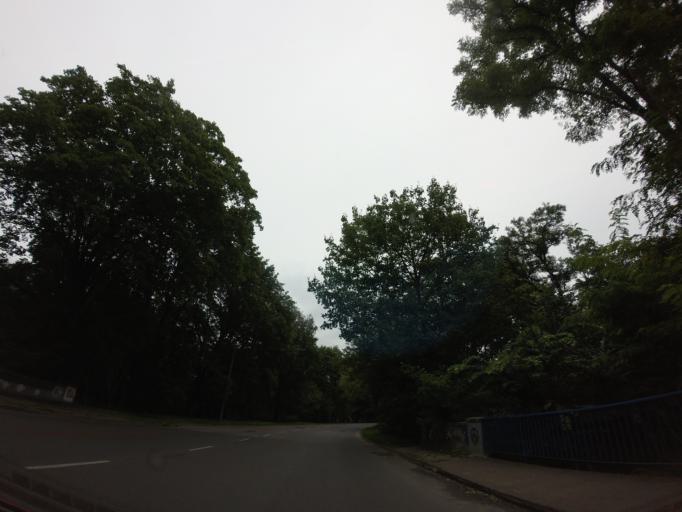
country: PL
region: West Pomeranian Voivodeship
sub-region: Szczecin
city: Szczecin
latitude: 53.4602
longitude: 14.5042
